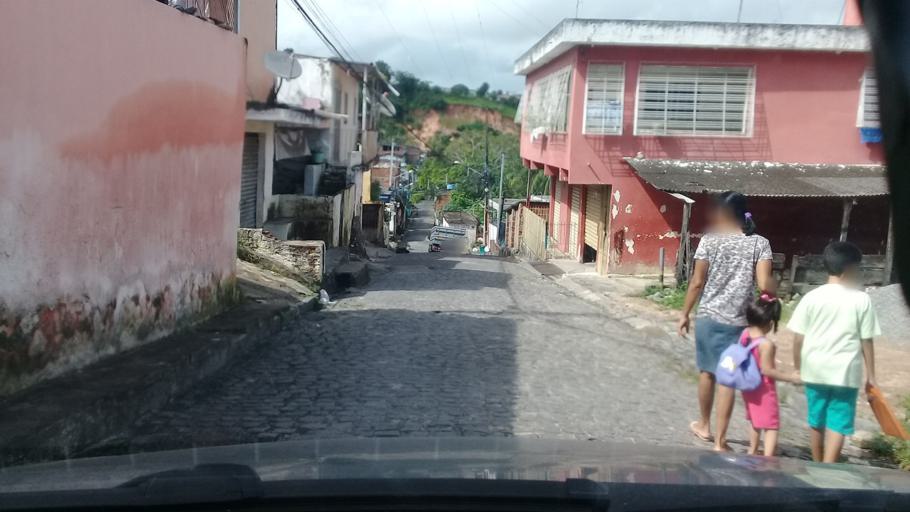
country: BR
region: Pernambuco
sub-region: Jaboatao Dos Guararapes
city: Jaboatao dos Guararapes
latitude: -8.1136
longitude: -34.9660
